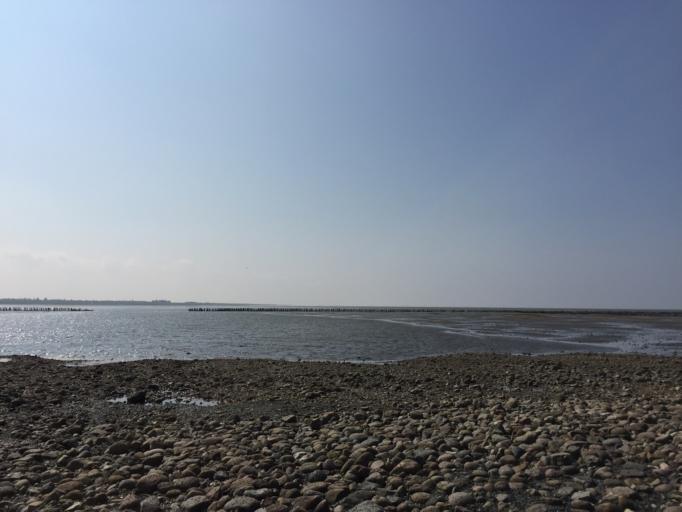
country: DK
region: South Denmark
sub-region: Esbjerg Kommune
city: Ribe
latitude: 55.3093
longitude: 8.6408
